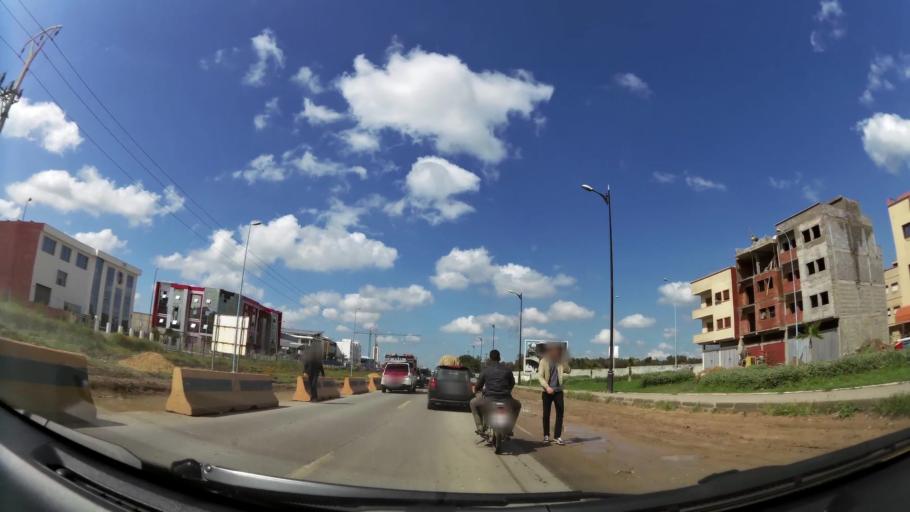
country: MA
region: Grand Casablanca
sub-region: Mediouna
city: Mediouna
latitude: 33.4012
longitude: -7.5343
